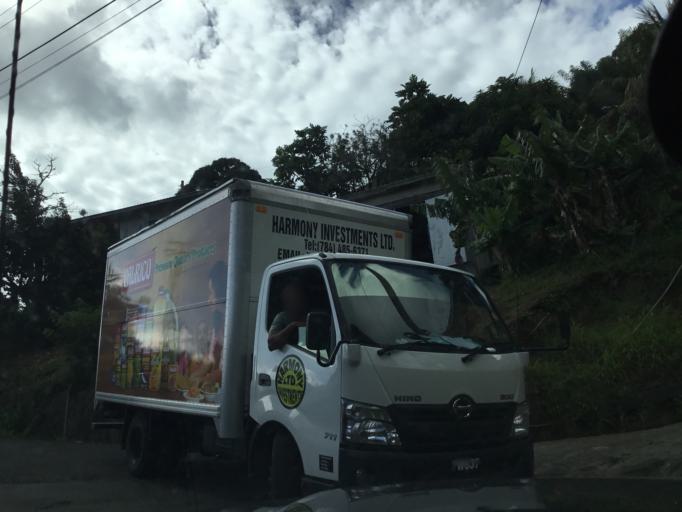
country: VC
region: Saint George
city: Kingstown
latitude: 13.1638
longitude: -61.2180
